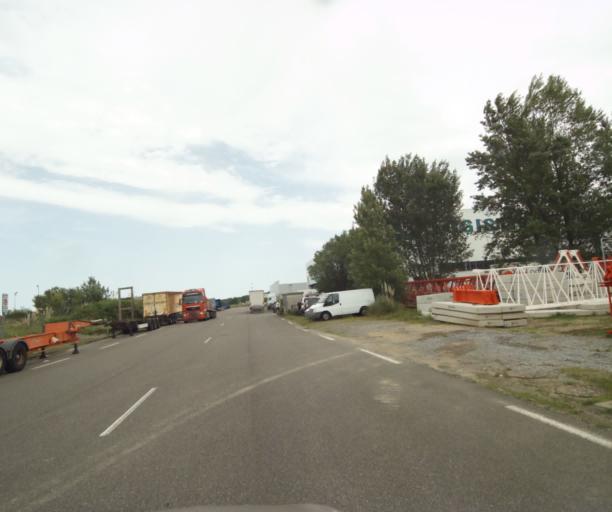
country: FR
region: Aquitaine
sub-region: Departement des Pyrenees-Atlantiques
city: Mouguerre
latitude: 43.4851
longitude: -1.4250
